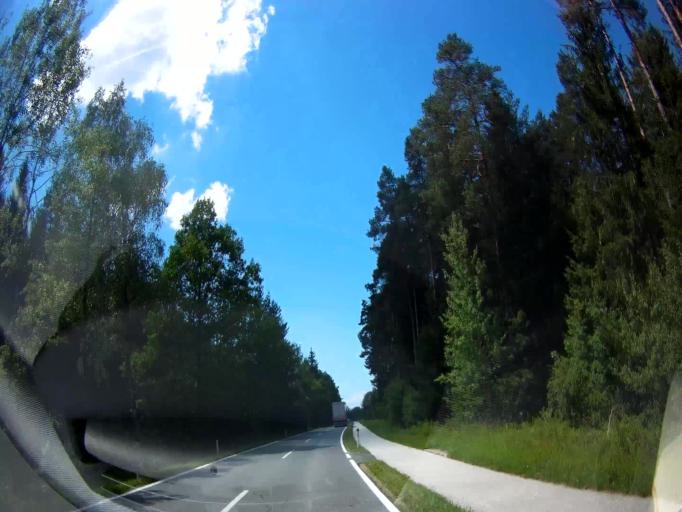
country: AT
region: Carinthia
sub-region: Politischer Bezirk Volkermarkt
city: Globasnitz
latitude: 46.6071
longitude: 14.6958
